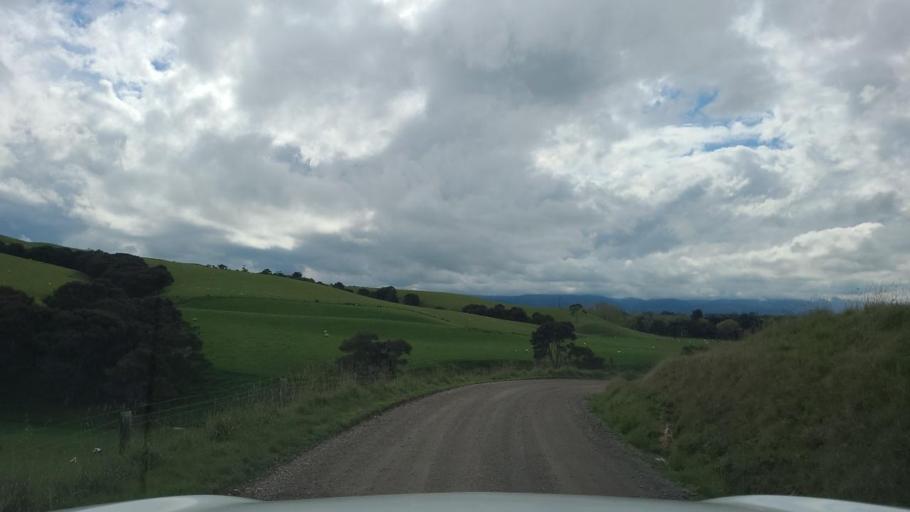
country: NZ
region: Wellington
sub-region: Masterton District
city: Masterton
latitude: -41.1046
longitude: 175.5392
